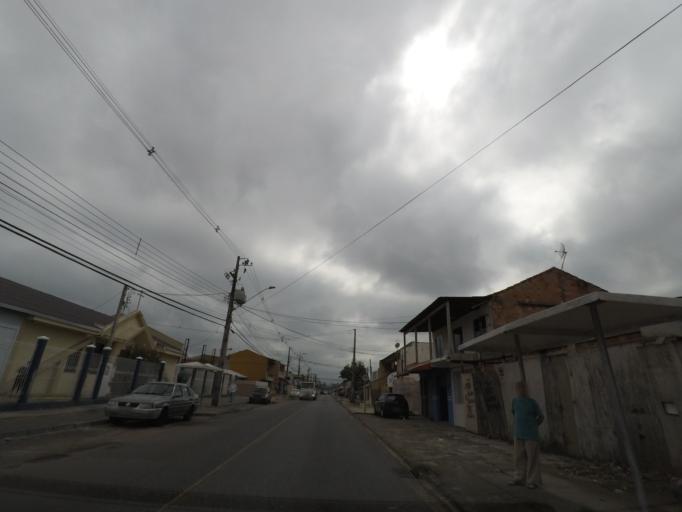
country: BR
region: Parana
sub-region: Curitiba
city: Curitiba
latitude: -25.5059
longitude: -49.3379
